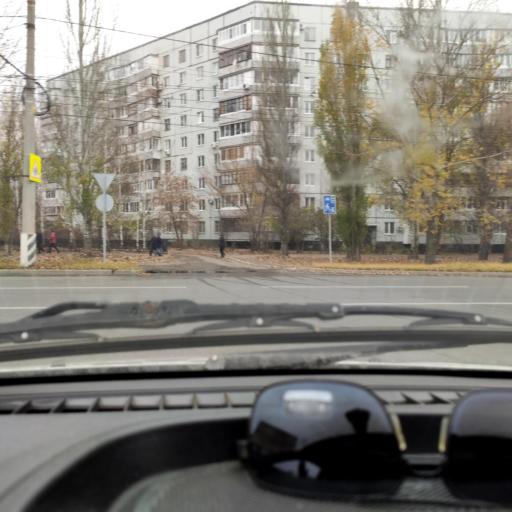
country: RU
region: Samara
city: Tol'yatti
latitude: 53.5063
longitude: 49.4408
